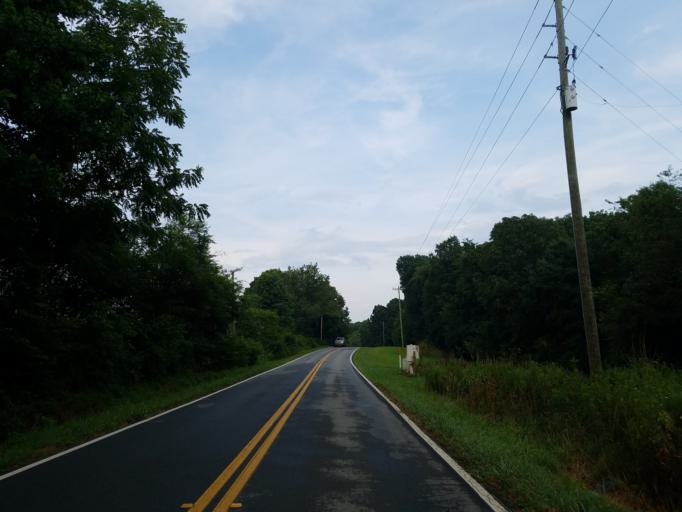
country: US
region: Georgia
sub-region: Pickens County
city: Jasper
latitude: 34.4572
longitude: -84.5390
